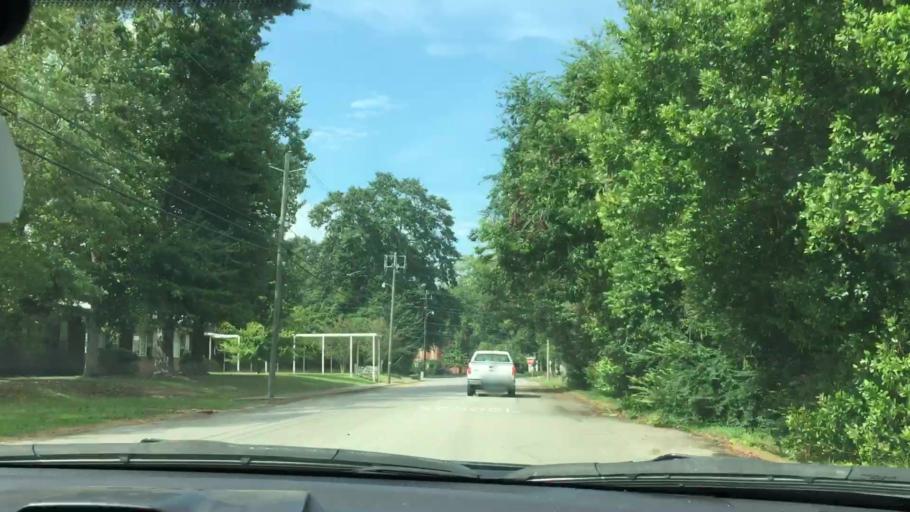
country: US
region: Alabama
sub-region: Hale County
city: Greensboro
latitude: 32.7019
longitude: -87.5991
